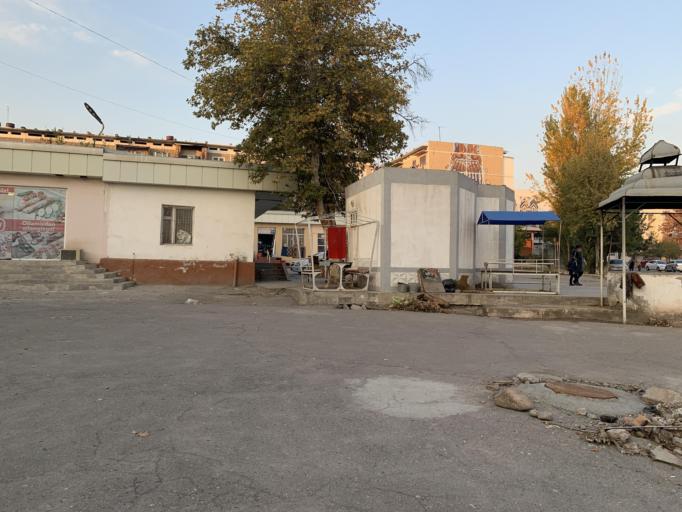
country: UZ
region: Namangan
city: Namangan Shahri
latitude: 41.0049
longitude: 71.5992
